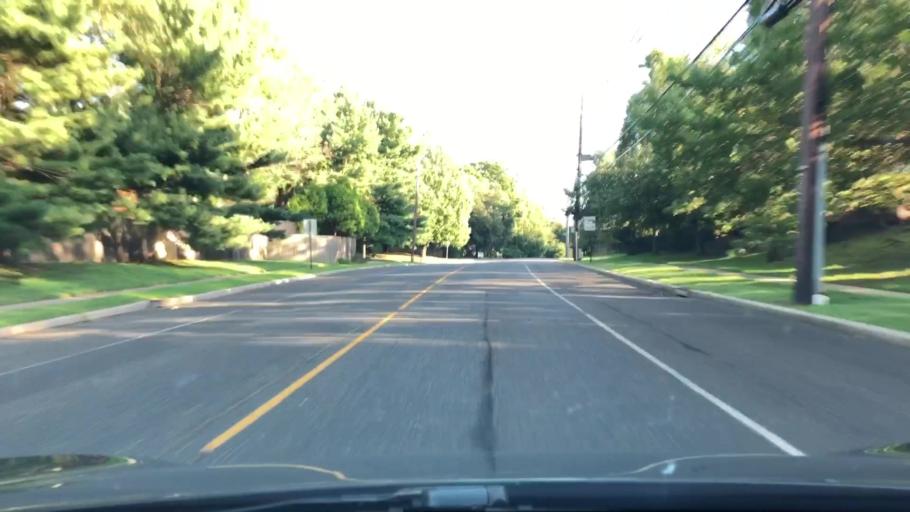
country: US
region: New Jersey
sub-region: Mercer County
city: Lawrenceville
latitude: 40.3074
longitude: -74.7313
